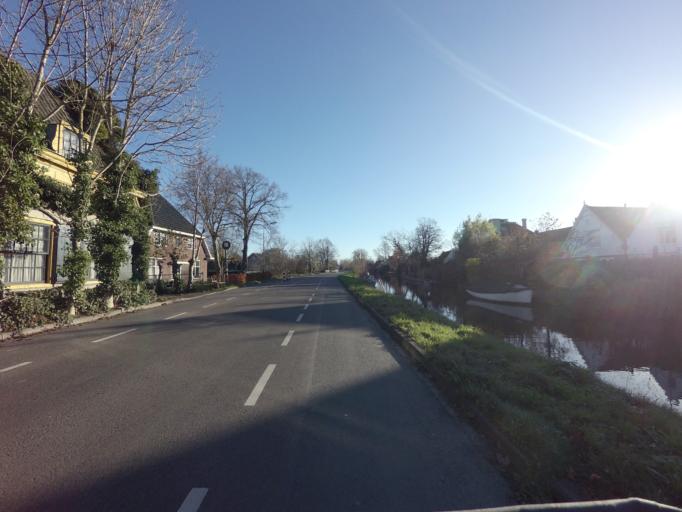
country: NL
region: Utrecht
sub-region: Stichtse Vecht
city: Vreeland
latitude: 52.2459
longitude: 4.9912
